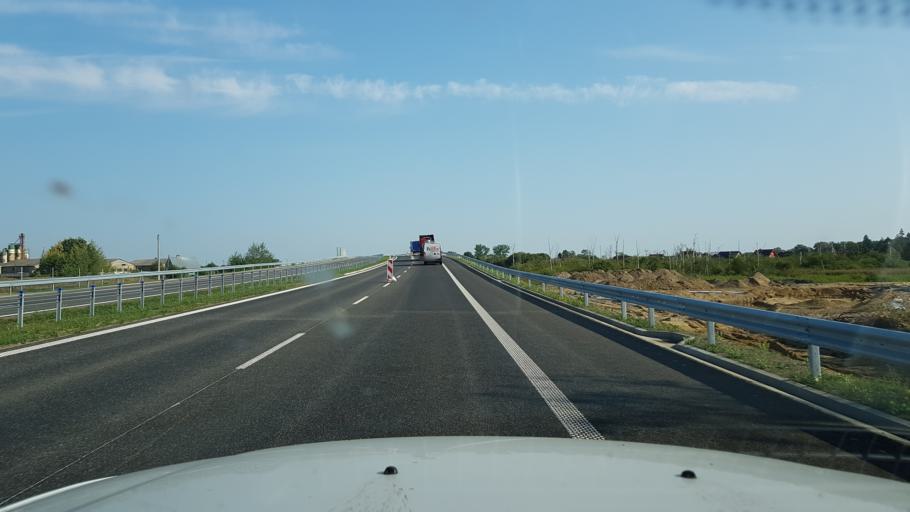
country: PL
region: West Pomeranian Voivodeship
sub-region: Powiat gryficki
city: Ploty
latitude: 53.7937
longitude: 15.2526
